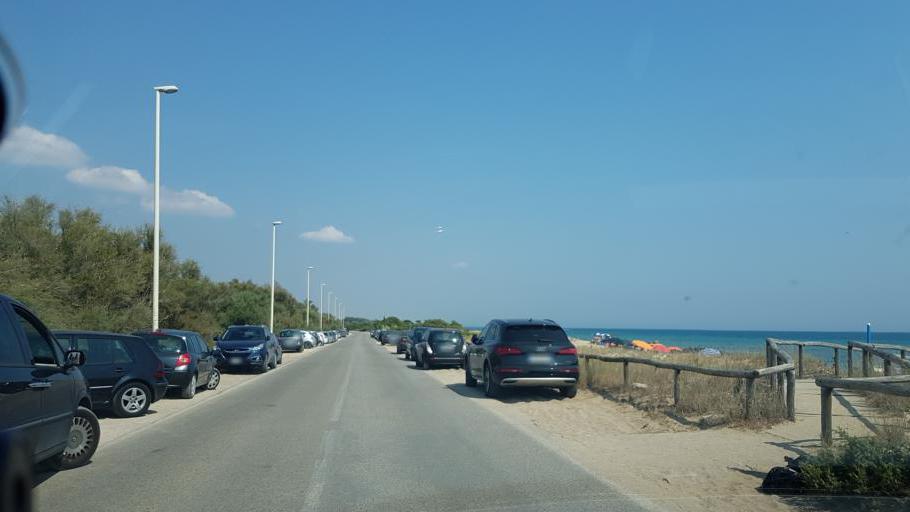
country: IT
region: Apulia
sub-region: Provincia di Taranto
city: Maruggio
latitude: 40.3022
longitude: 17.6227
